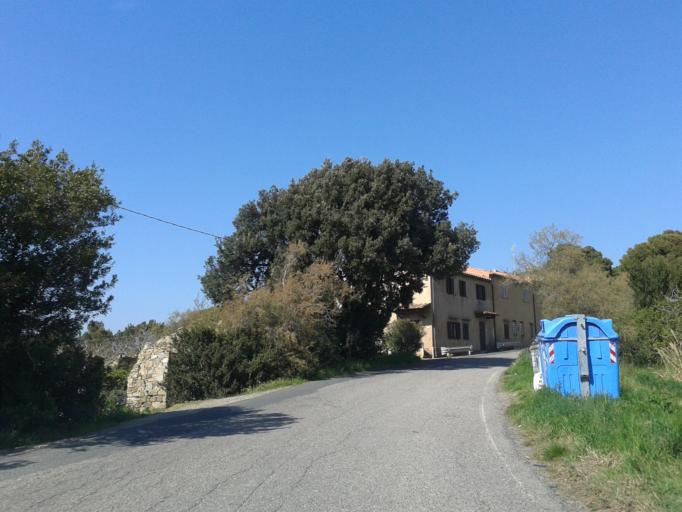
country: IT
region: Tuscany
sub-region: Provincia di Livorno
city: Quercianella
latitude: 43.4544
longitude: 10.4029
